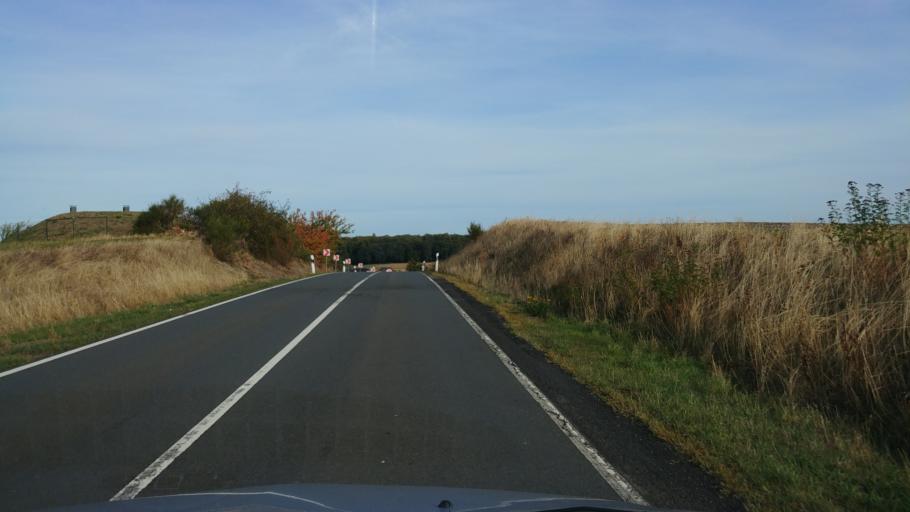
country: DE
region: Rheinland-Pfalz
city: Reckenroth
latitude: 50.1872
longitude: 8.0102
